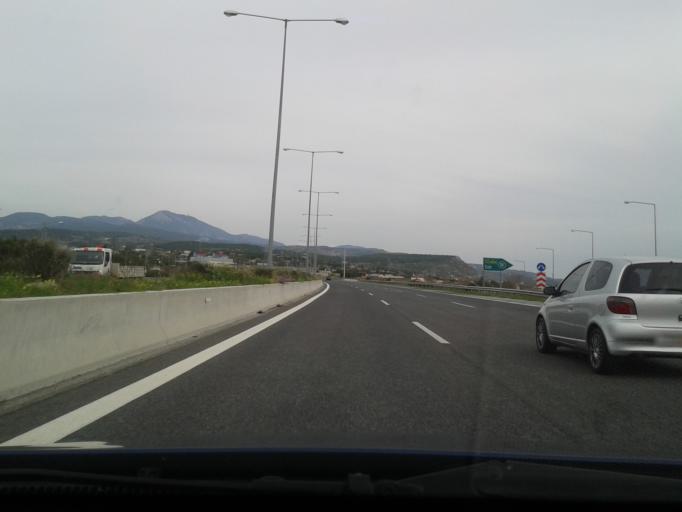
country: GR
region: Peloponnese
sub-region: Nomos Korinthias
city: Kyras Vrysi
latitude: 37.9206
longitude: 22.9883
